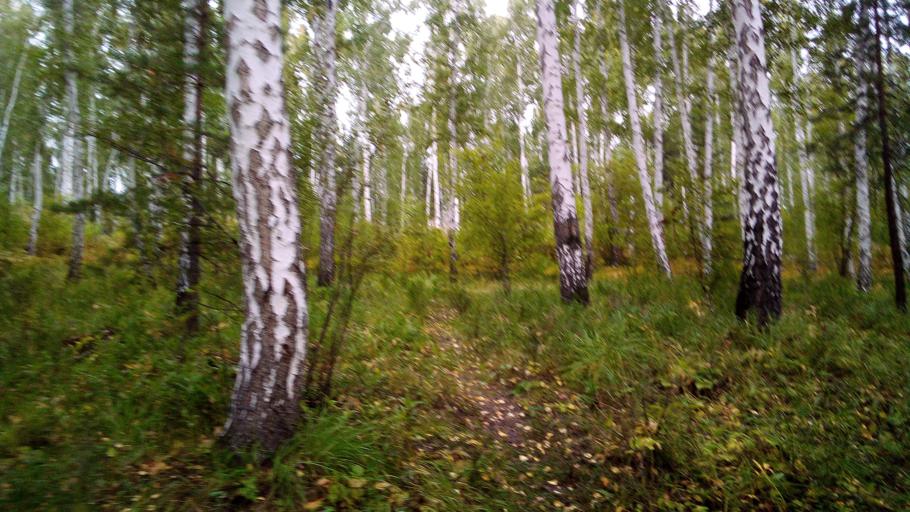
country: RU
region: Chelyabinsk
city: Tayginka
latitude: 55.4753
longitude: 60.4965
